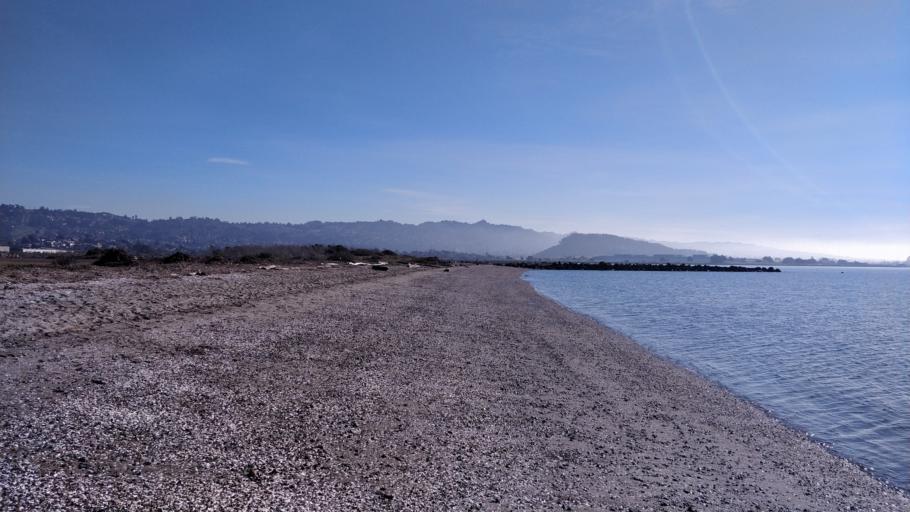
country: US
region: California
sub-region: Contra Costa County
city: El Cerrito
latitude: 37.9089
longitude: -122.3390
